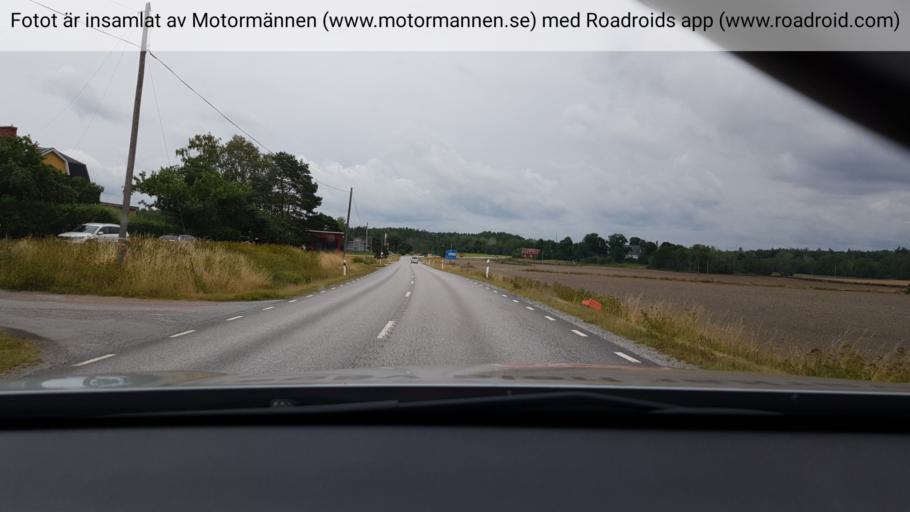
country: SE
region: Stockholm
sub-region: Vallentuna Kommun
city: Vallentuna
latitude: 59.6730
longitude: 18.0453
